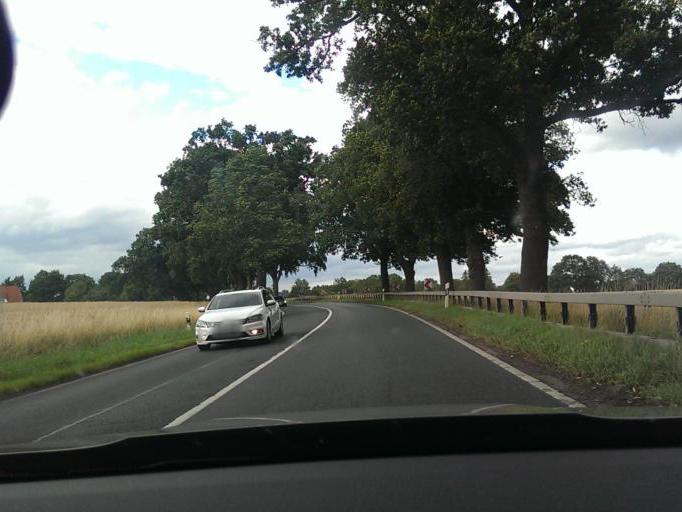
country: DE
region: Lower Saxony
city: Elze
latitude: 52.5372
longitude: 9.7293
